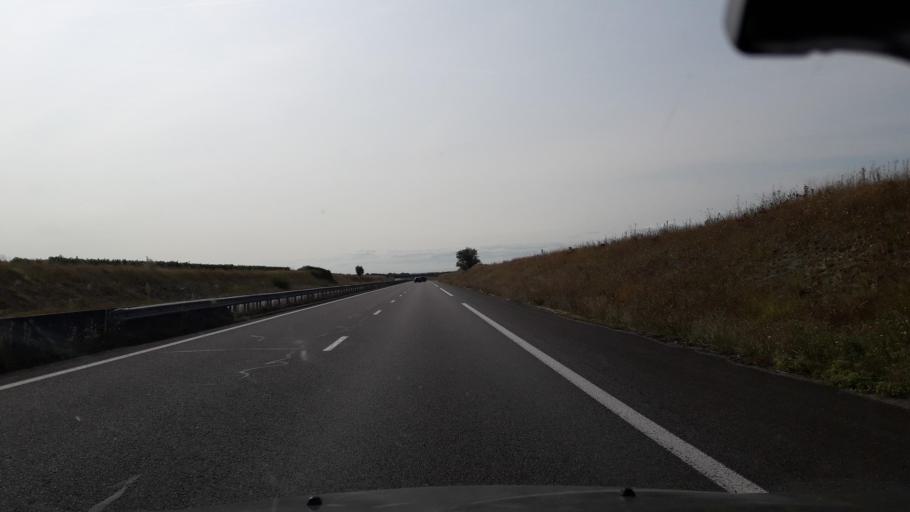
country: FR
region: Poitou-Charentes
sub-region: Departement de la Charente
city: Saint-Meme-les-Carrieres
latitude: 45.6963
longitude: -0.1129
